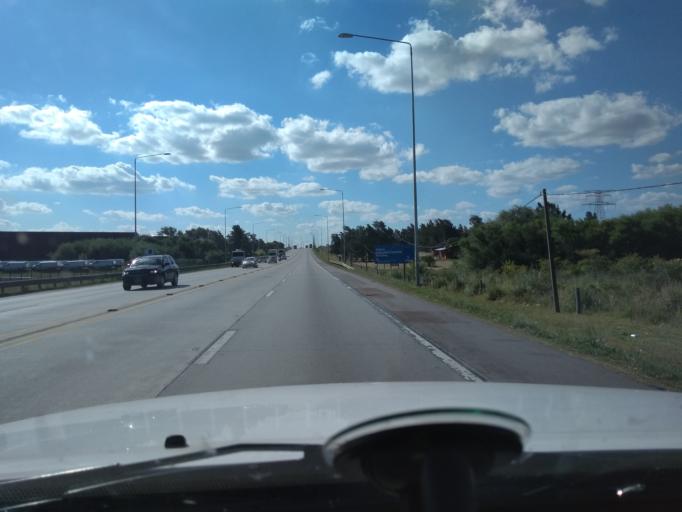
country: UY
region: Canelones
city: La Paz
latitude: -34.7878
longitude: -56.2178
